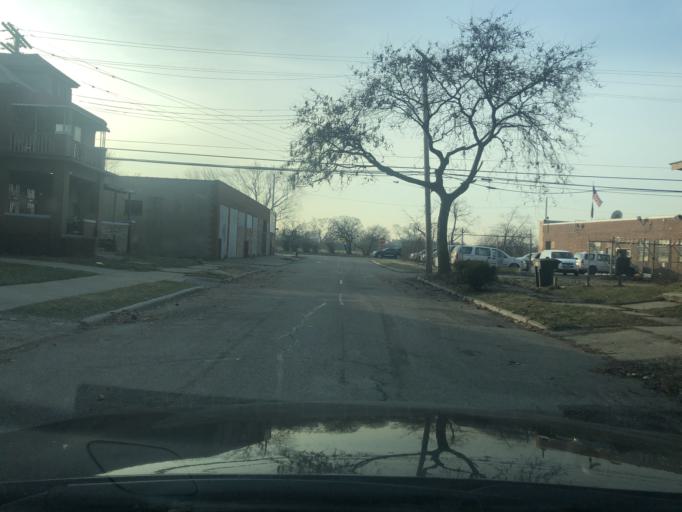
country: US
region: Michigan
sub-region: Wayne County
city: Highland Park
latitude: 42.4036
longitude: -83.1284
